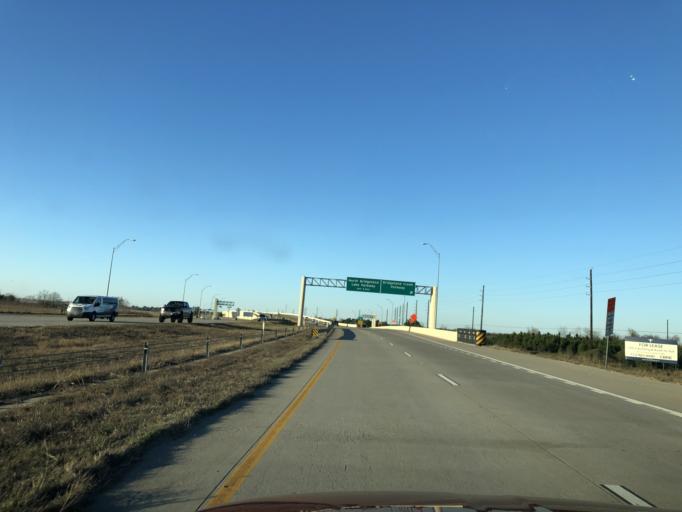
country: US
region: Texas
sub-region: Harris County
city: Cypress
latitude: 29.9350
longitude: -95.7637
